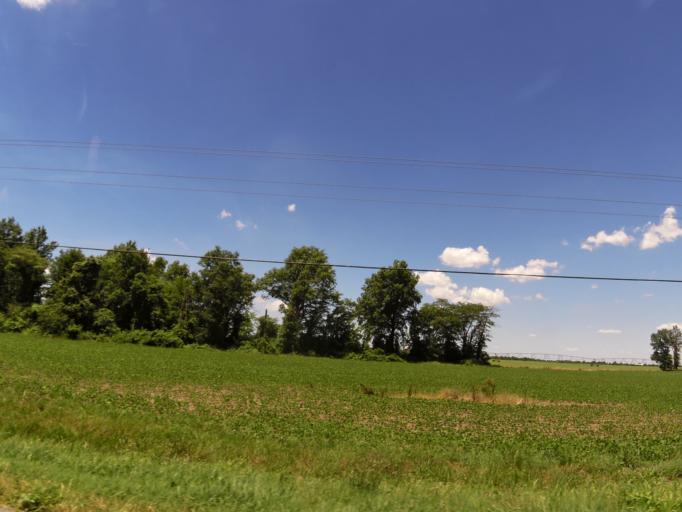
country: US
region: Missouri
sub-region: New Madrid County
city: New Madrid
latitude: 36.5788
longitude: -89.5604
